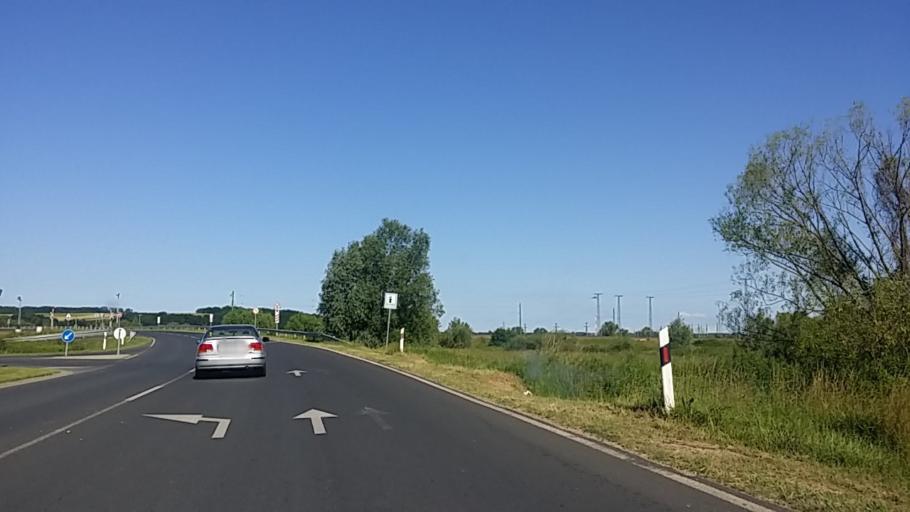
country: HU
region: Zala
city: Zalaegerszeg
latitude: 46.8572
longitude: 16.7910
